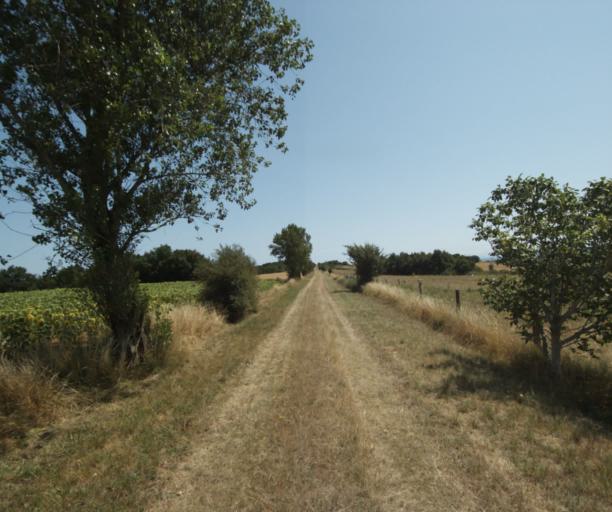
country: FR
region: Midi-Pyrenees
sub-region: Departement de la Haute-Garonne
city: Saint-Felix-Lauragais
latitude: 43.4464
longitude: 1.8620
